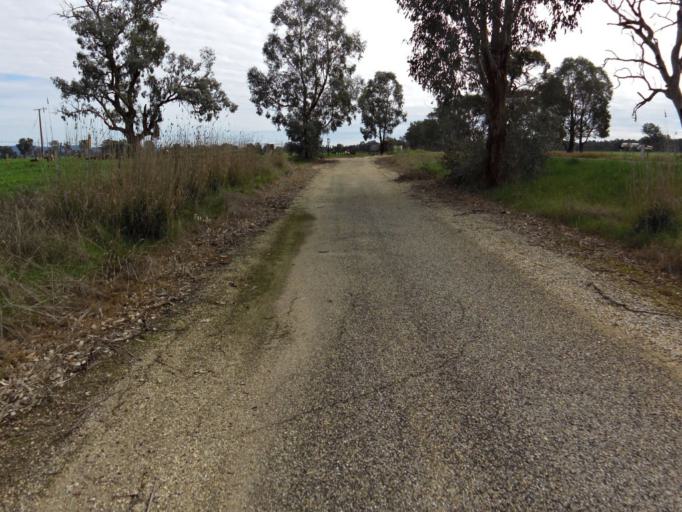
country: AU
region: Victoria
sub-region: Wangaratta
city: Wangaratta
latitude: -36.4177
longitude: 146.3553
